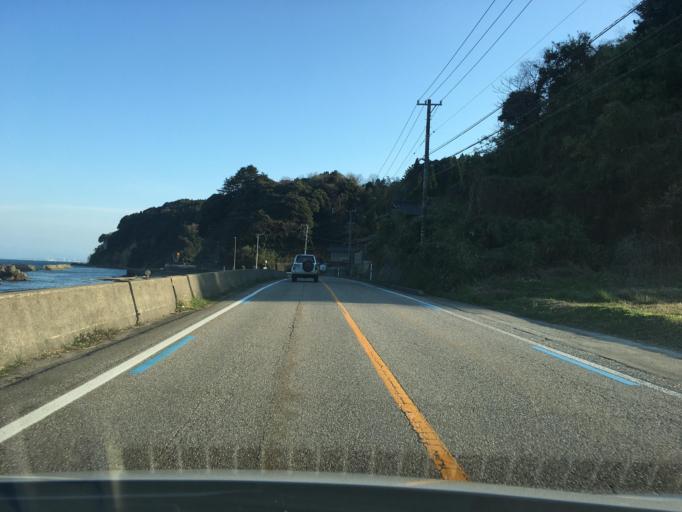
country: JP
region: Toyama
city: Himi
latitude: 36.9368
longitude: 137.0268
